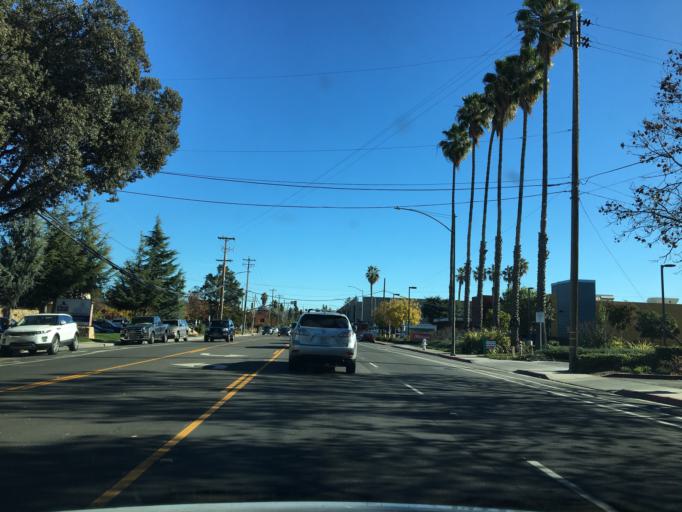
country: US
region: California
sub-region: Santa Clara County
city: Mountain View
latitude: 37.4217
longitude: -122.0985
